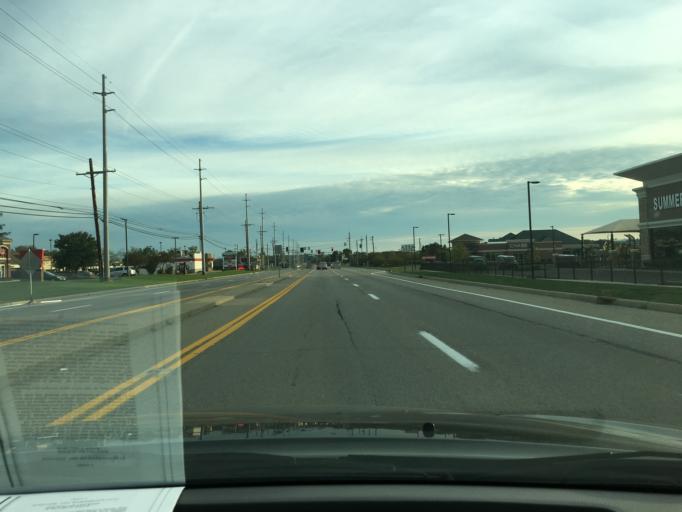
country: US
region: Ohio
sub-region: Butler County
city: Beckett Ridge
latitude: 39.3565
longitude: -84.4611
